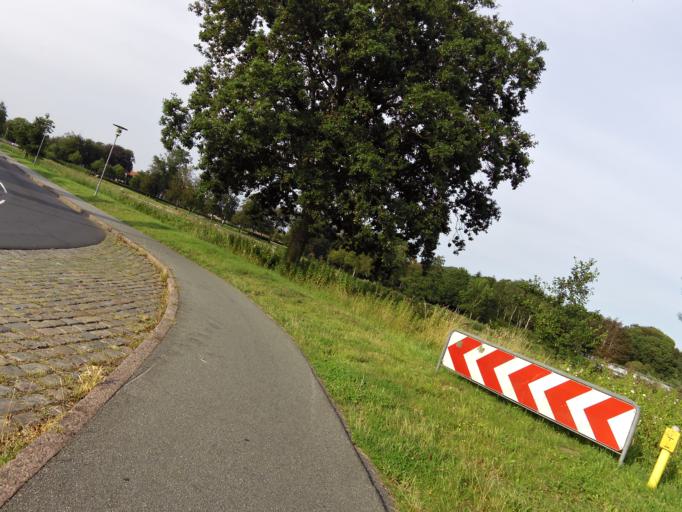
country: DK
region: South Denmark
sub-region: Esbjerg Kommune
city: Ribe
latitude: 55.3254
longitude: 8.7672
